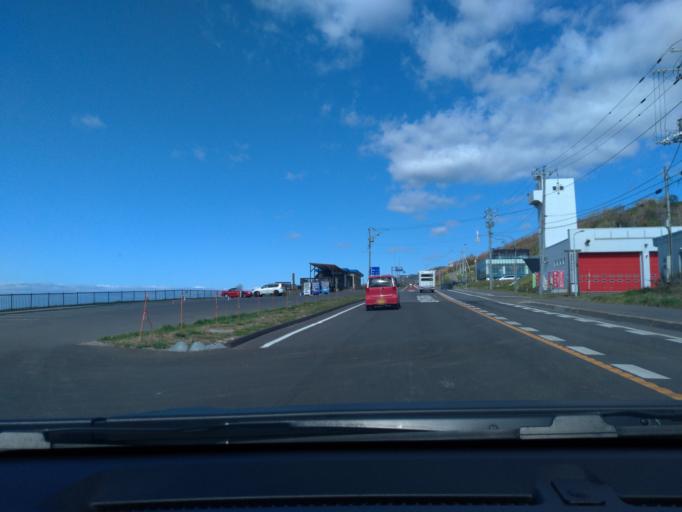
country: JP
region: Hokkaido
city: Ishikari
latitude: 43.4024
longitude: 141.4314
